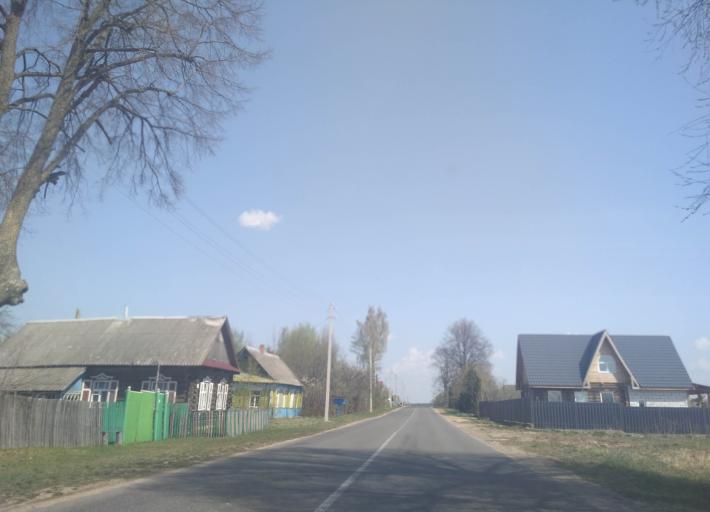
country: BY
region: Minsk
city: Loshnitsa
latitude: 54.4083
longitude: 28.6255
